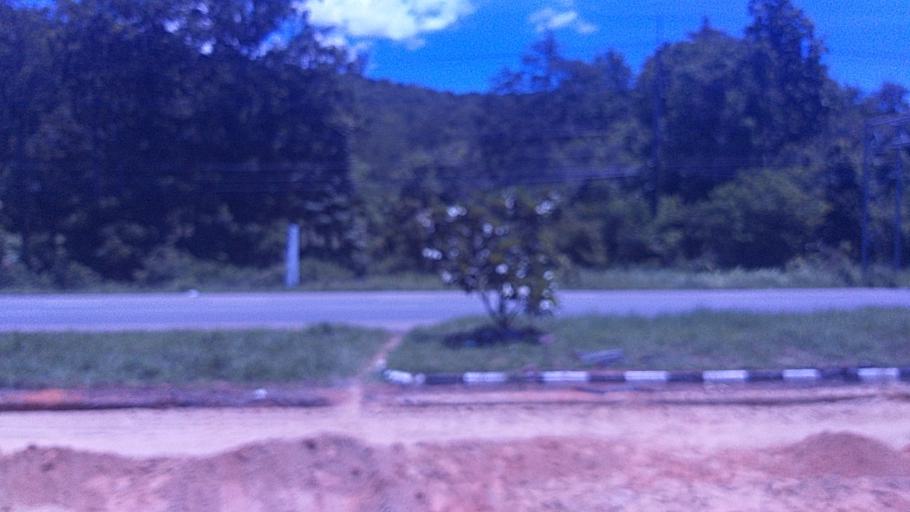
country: TH
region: Chaiyaphum
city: Kaeng Khro
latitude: 16.0660
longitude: 102.2775
